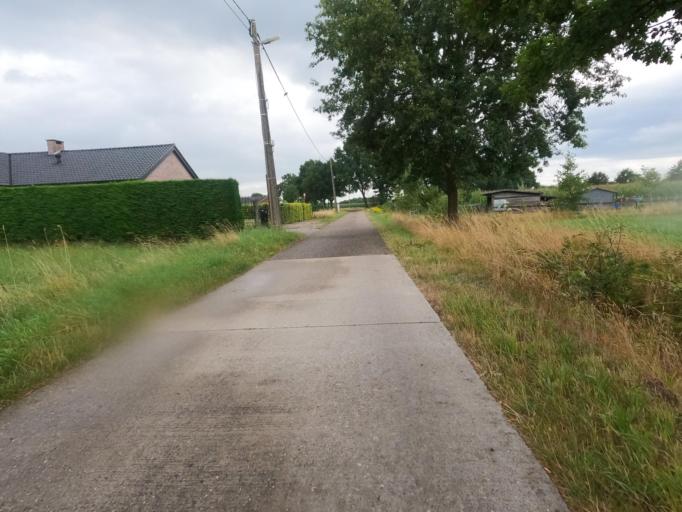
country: BE
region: Flanders
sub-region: Provincie Antwerpen
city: Rijkevorsel
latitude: 51.3597
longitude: 4.7437
